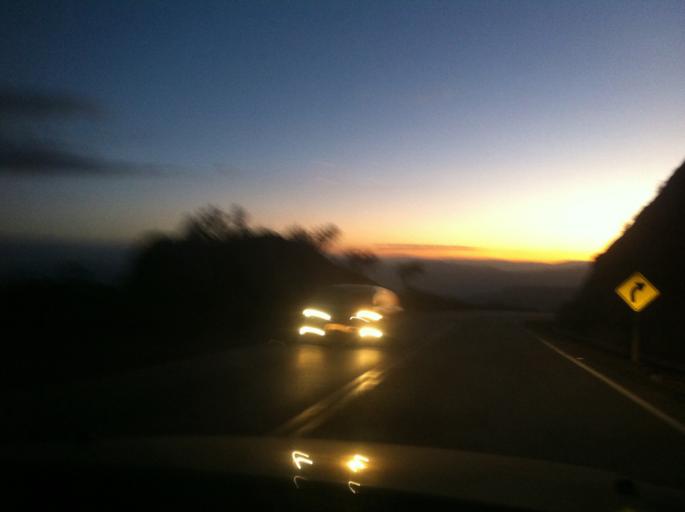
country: BO
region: Cochabamba
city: Irpa Irpa
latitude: -17.6651
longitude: -66.4477
